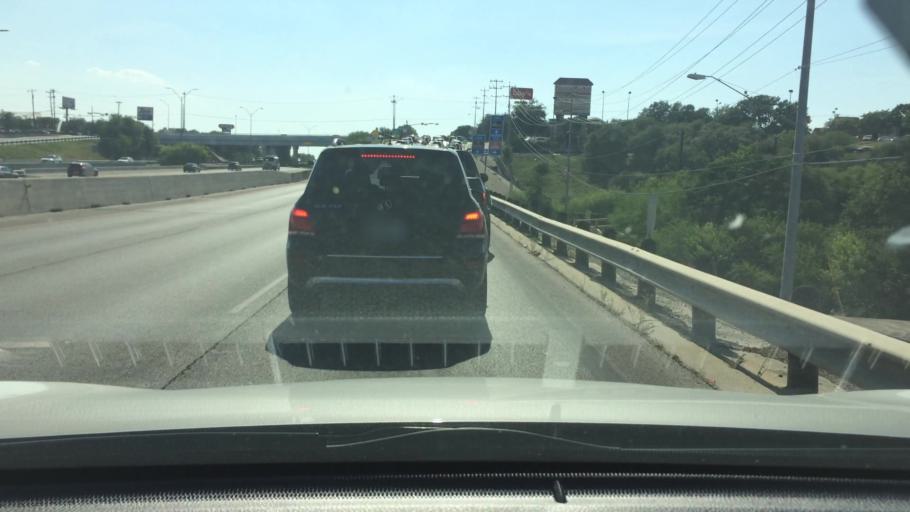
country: US
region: Texas
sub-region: Bexar County
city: Hollywood Park
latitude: 29.6091
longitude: -98.5055
